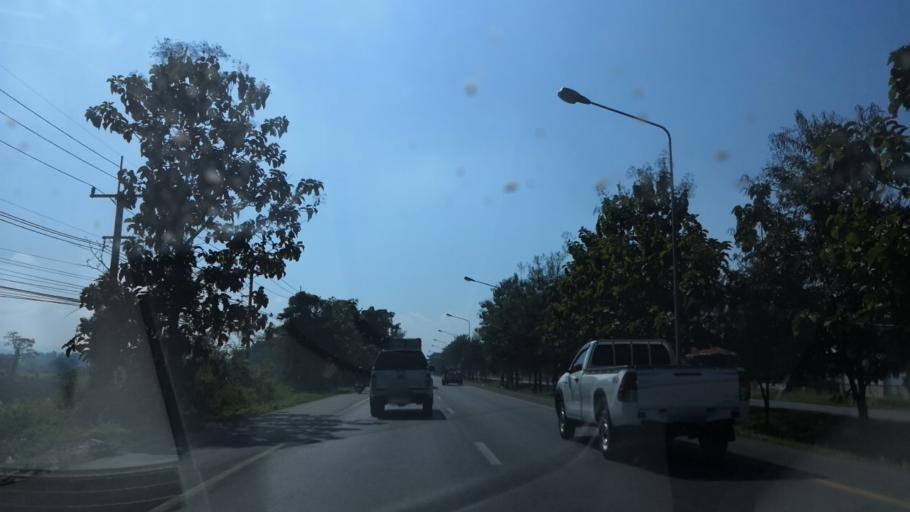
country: TH
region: Chiang Rai
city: Mae Lao
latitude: 19.7919
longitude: 99.7483
